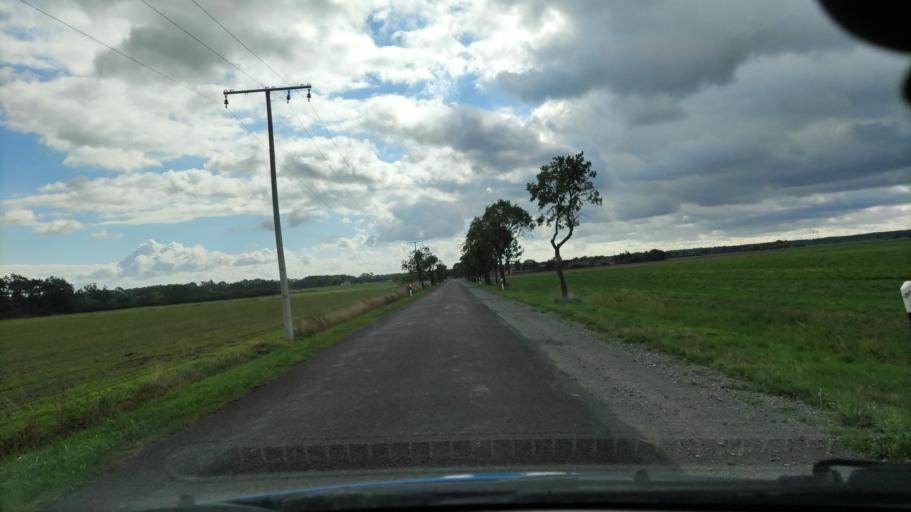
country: DE
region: Saxony-Anhalt
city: Pretzier
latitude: 52.8358
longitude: 11.3484
